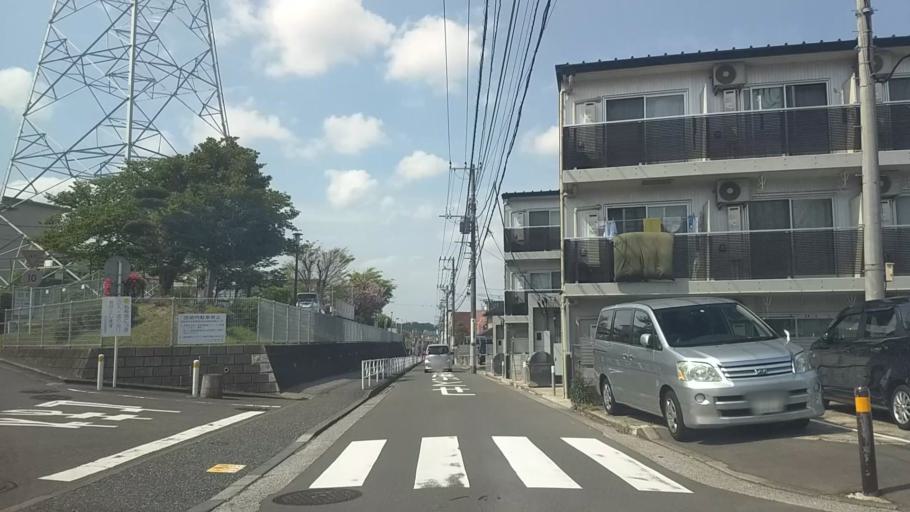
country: JP
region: Kanagawa
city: Kamakura
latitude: 35.3721
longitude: 139.5769
